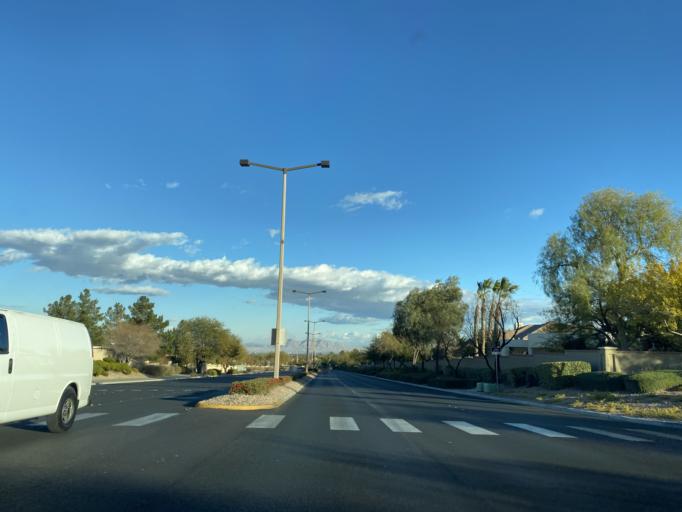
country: US
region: Nevada
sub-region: Clark County
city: Summerlin South
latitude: 36.2045
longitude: -115.3143
